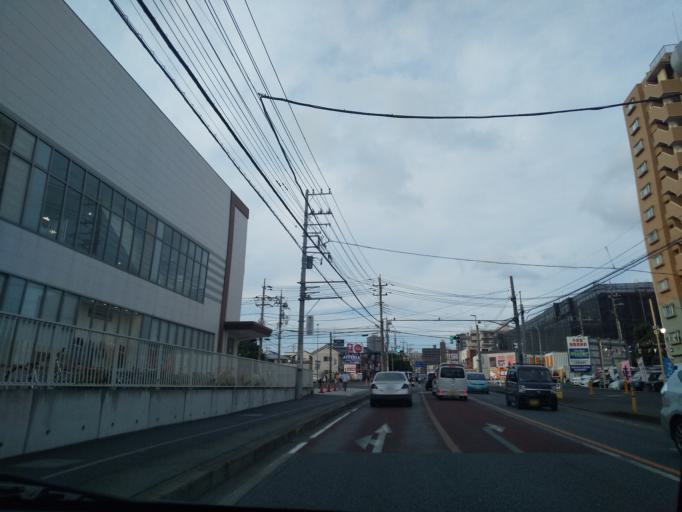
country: JP
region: Kanagawa
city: Zama
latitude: 35.5077
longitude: 139.4138
